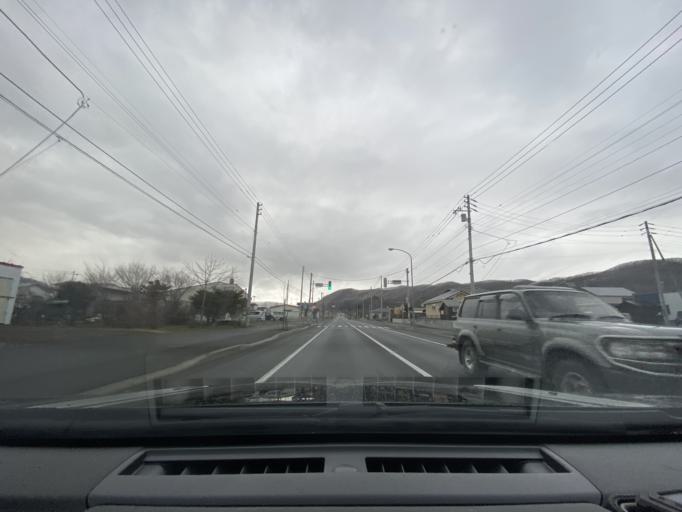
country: JP
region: Hokkaido
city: Otofuke
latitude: 43.2504
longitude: 143.5474
